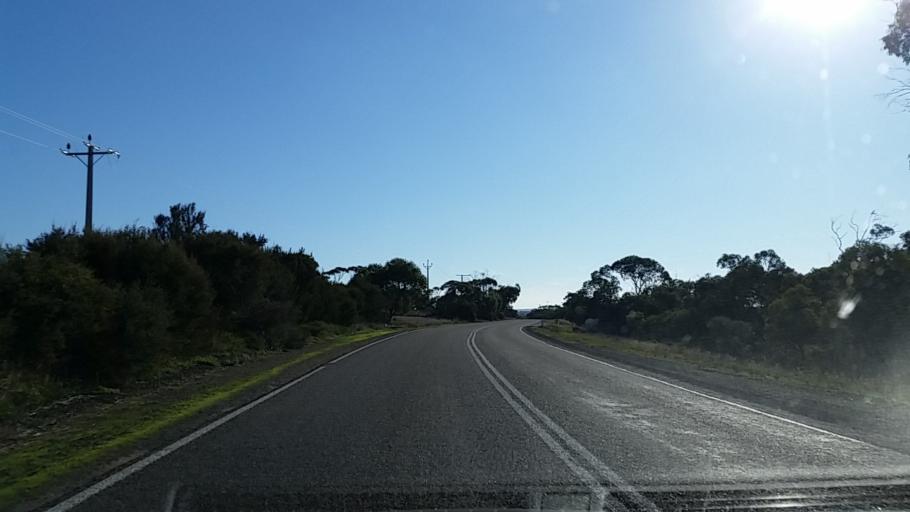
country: AU
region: South Australia
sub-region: Murray Bridge
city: Murray Bridge
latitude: -35.1231
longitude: 139.1775
